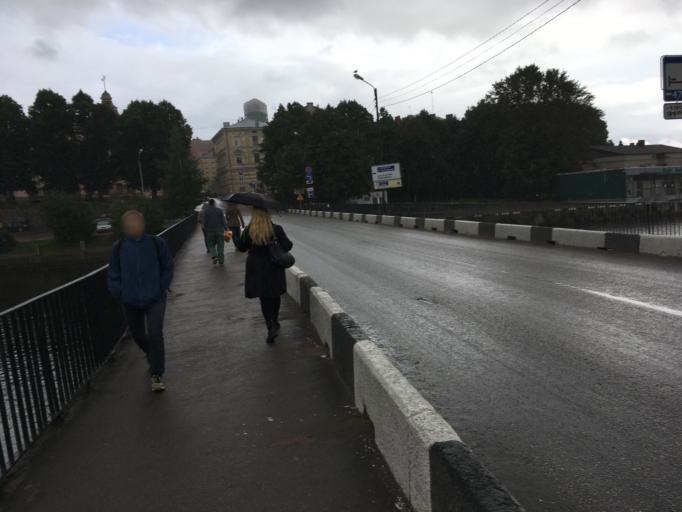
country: RU
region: Leningrad
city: Vyborg
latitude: 60.7149
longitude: 28.7283
